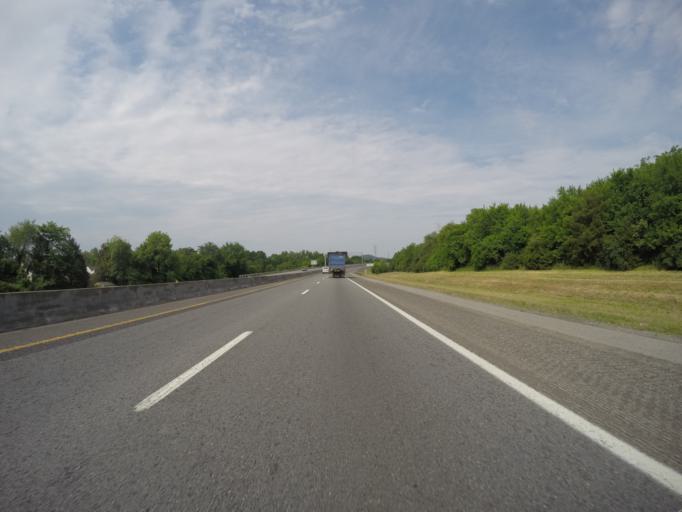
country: US
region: Tennessee
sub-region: Davidson County
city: Nashville
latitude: 36.2353
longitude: -86.7985
